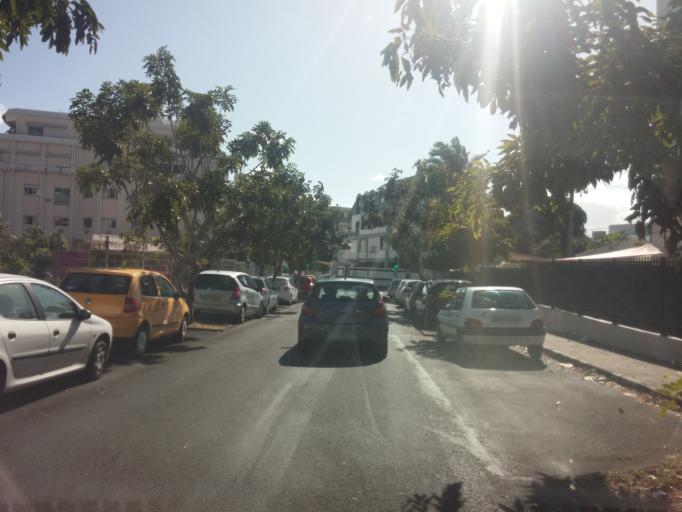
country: RE
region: Reunion
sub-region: Reunion
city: Saint-Denis
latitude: -20.8863
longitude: 55.4468
